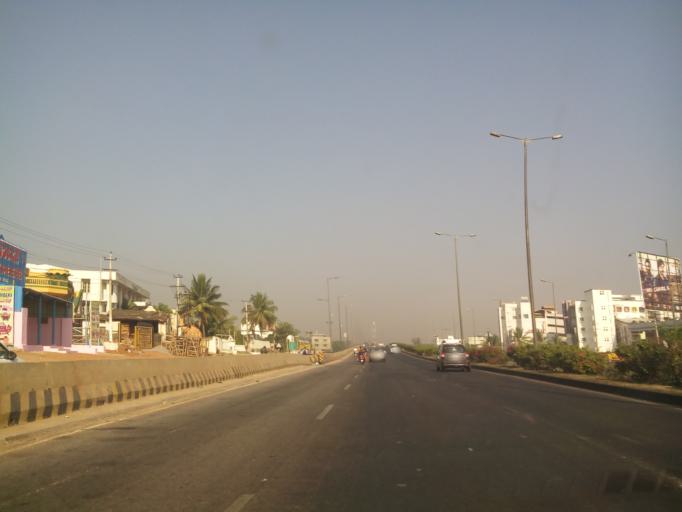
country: IN
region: Karnataka
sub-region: Bangalore Rural
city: Nelamangala
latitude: 13.0916
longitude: 77.3977
